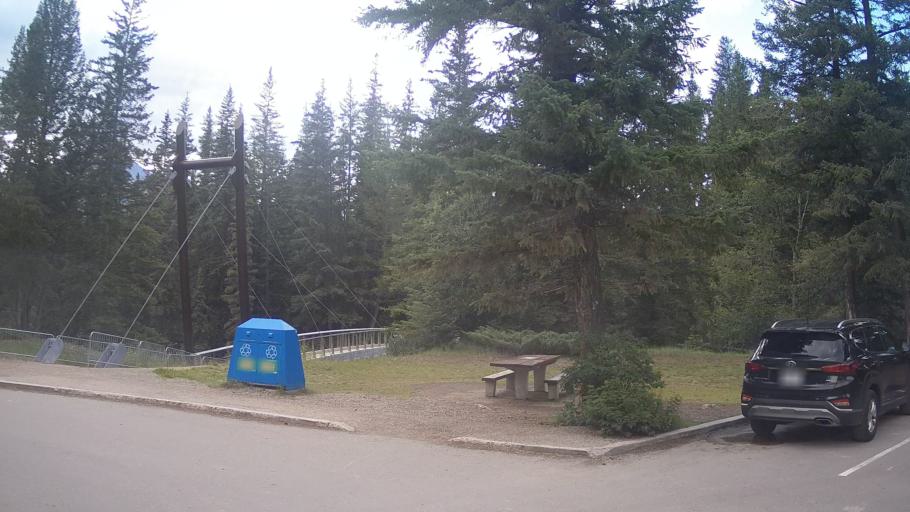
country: CA
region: Alberta
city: Jasper Park Lodge
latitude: 52.9213
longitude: -118.0163
